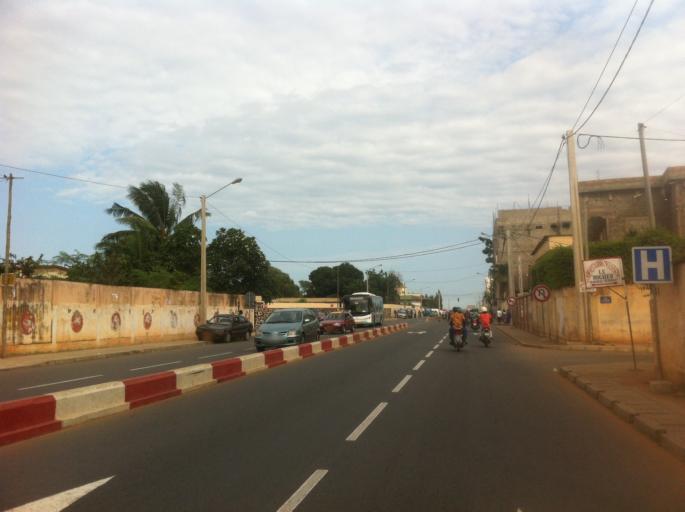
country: TG
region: Maritime
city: Lome
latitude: 6.1436
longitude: 1.2065
